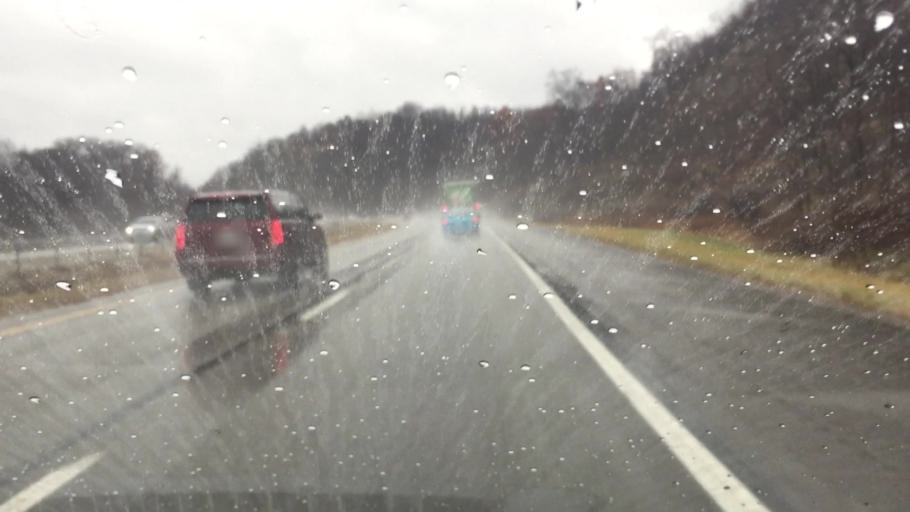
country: US
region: Pennsylvania
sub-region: Allegheny County
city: Franklin Park
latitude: 40.5553
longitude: -80.0850
